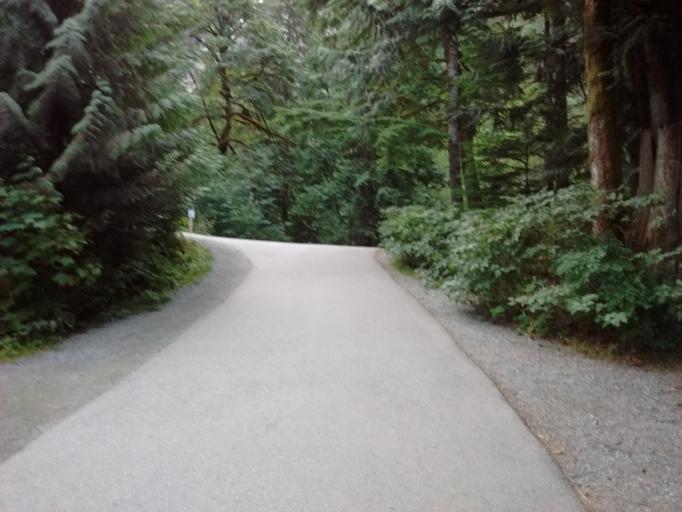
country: CA
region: British Columbia
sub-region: Greater Vancouver Regional District
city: Lions Bay
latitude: 49.6708
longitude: -123.1601
